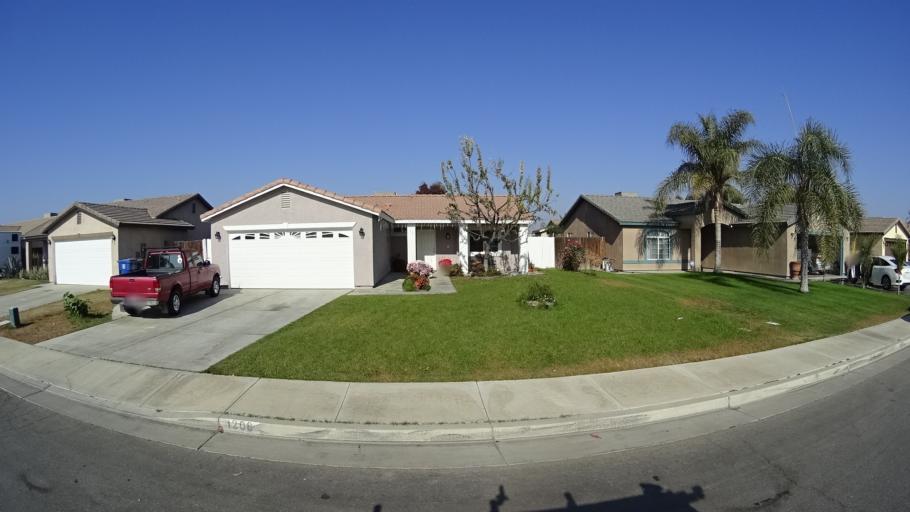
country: US
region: California
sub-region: Kern County
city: Greenfield
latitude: 35.2777
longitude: -119.0190
